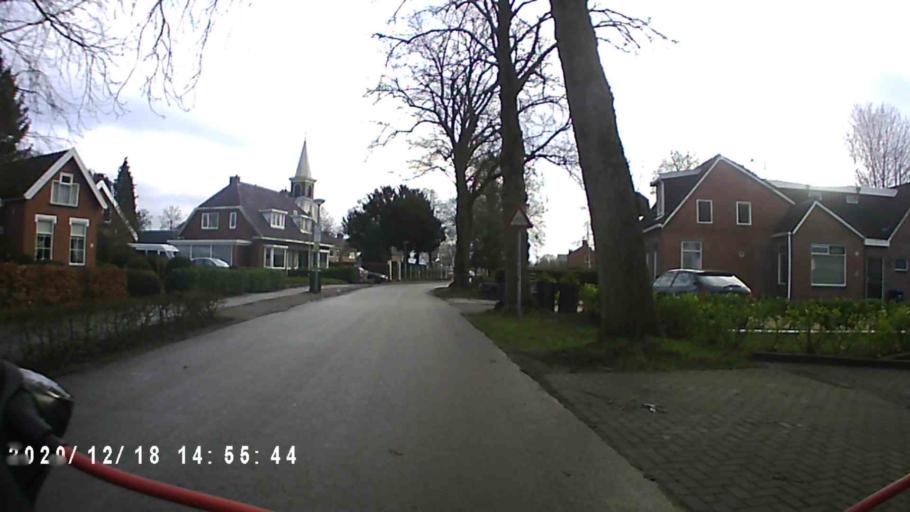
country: NL
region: Groningen
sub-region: Gemeente Haren
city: Haren
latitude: 53.1853
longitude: 6.6851
